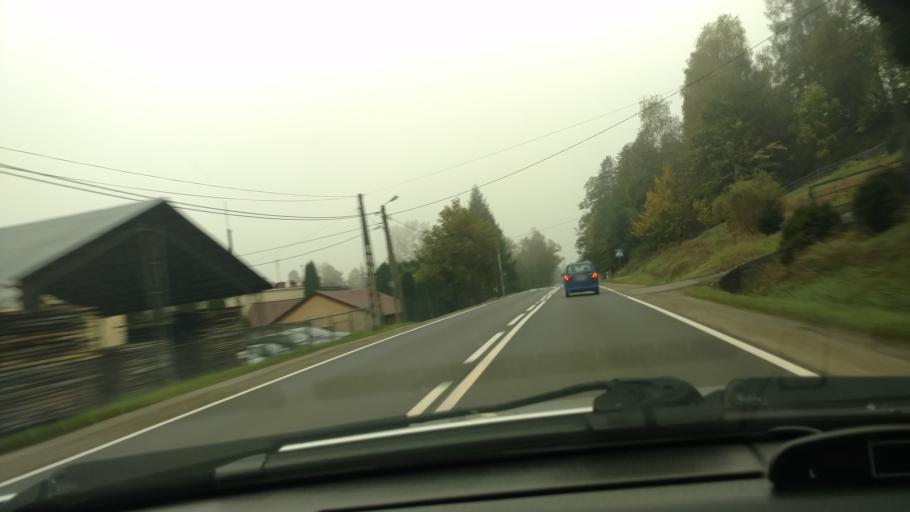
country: PL
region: Subcarpathian Voivodeship
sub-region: Powiat strzyzowski
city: Frysztak
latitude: 49.8355
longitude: 21.6124
